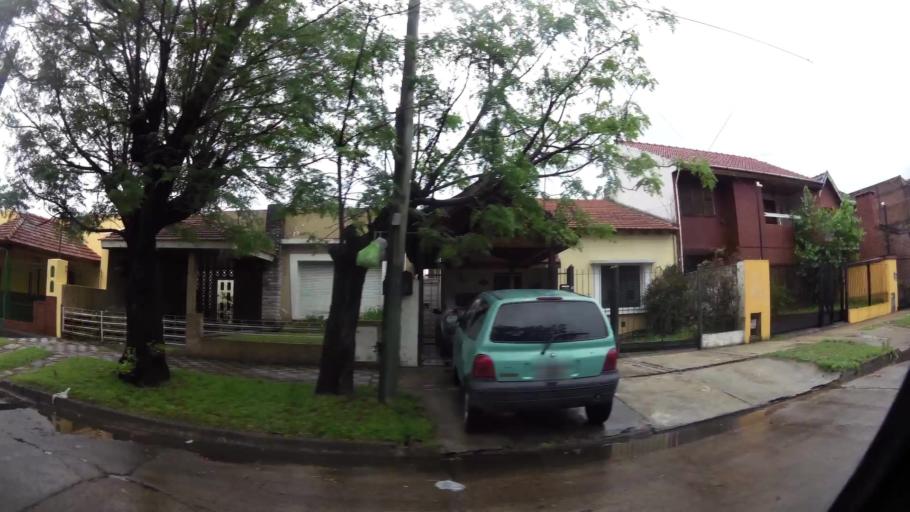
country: AR
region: Buenos Aires
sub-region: Partido de Lomas de Zamora
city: Lomas de Zamora
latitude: -34.7481
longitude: -58.3844
